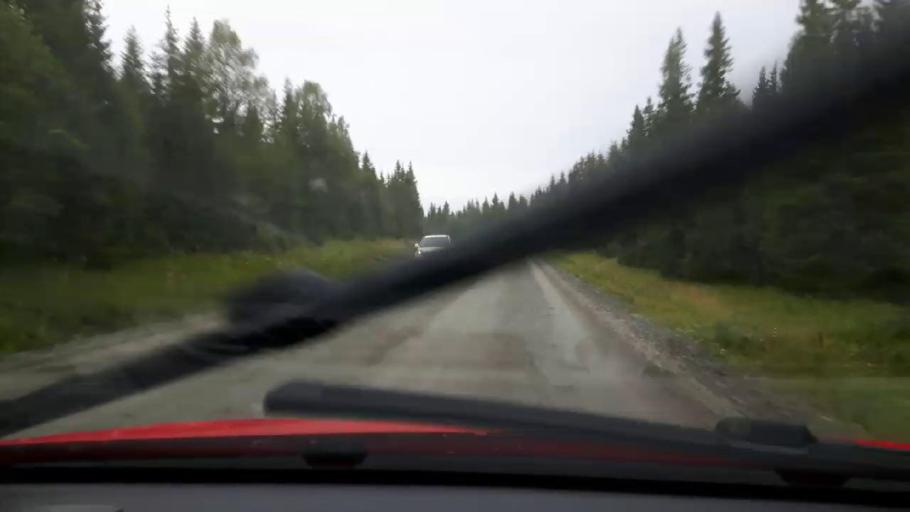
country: SE
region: Jaemtland
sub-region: Are Kommun
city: Are
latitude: 63.4511
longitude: 12.6534
